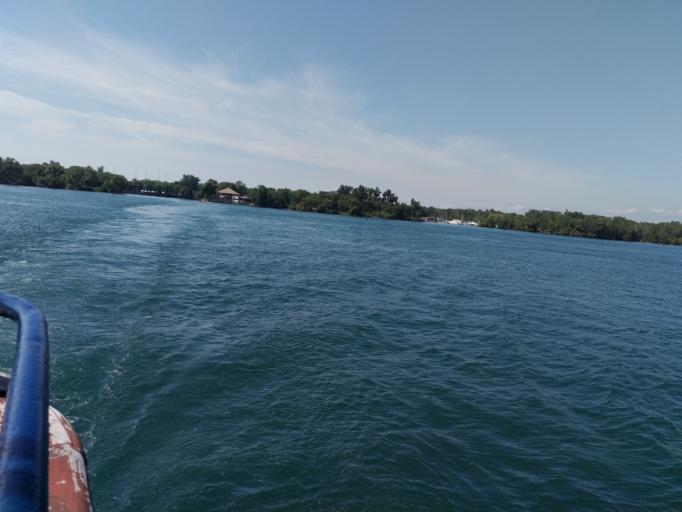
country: CA
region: Ontario
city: Toronto
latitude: 43.6278
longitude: -79.3751
